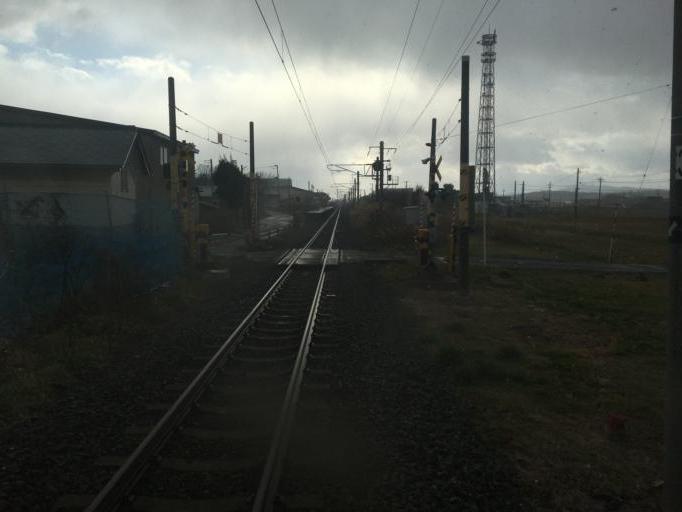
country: JP
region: Aomori
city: Aomori Shi
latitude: 40.9711
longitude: 140.6546
